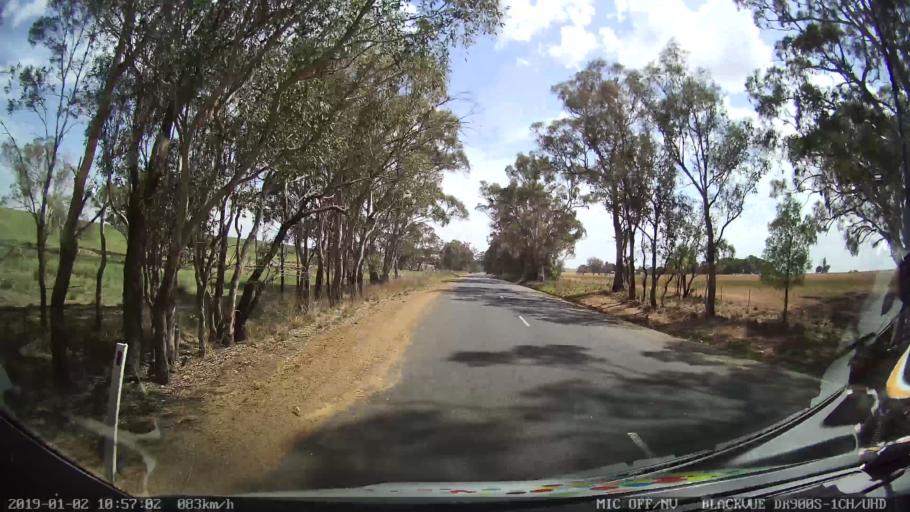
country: AU
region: New South Wales
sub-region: Cootamundra
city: Cootamundra
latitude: -34.6402
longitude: 148.2803
